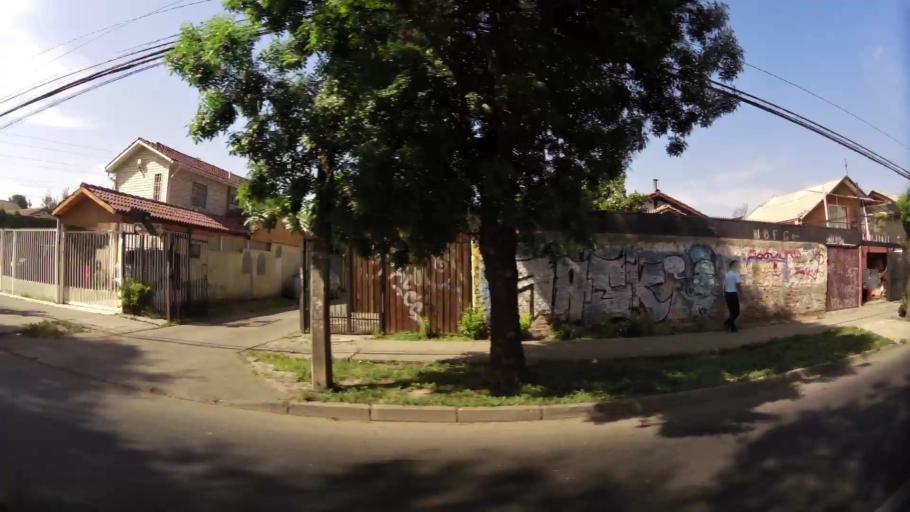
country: CL
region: Santiago Metropolitan
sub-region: Provincia de Santiago
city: Lo Prado
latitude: -33.4614
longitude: -70.7321
